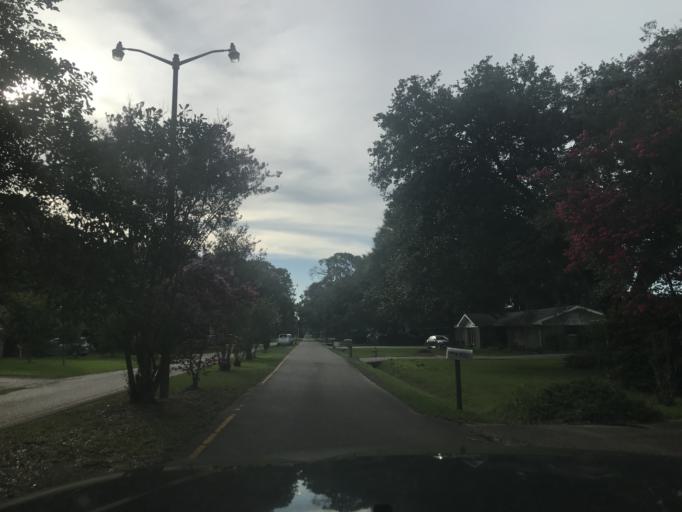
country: US
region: Louisiana
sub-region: Lafayette Parish
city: Lafayette
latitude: 30.1926
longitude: -92.0523
